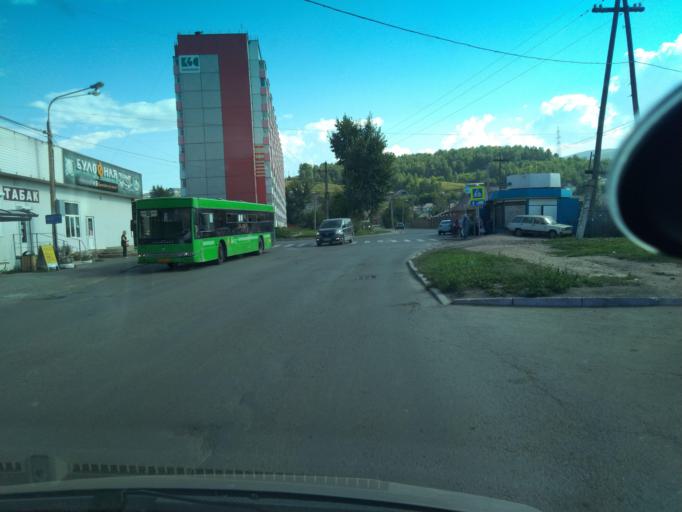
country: RU
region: Krasnoyarskiy
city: Krasnoyarsk
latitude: 55.9712
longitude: 92.9374
